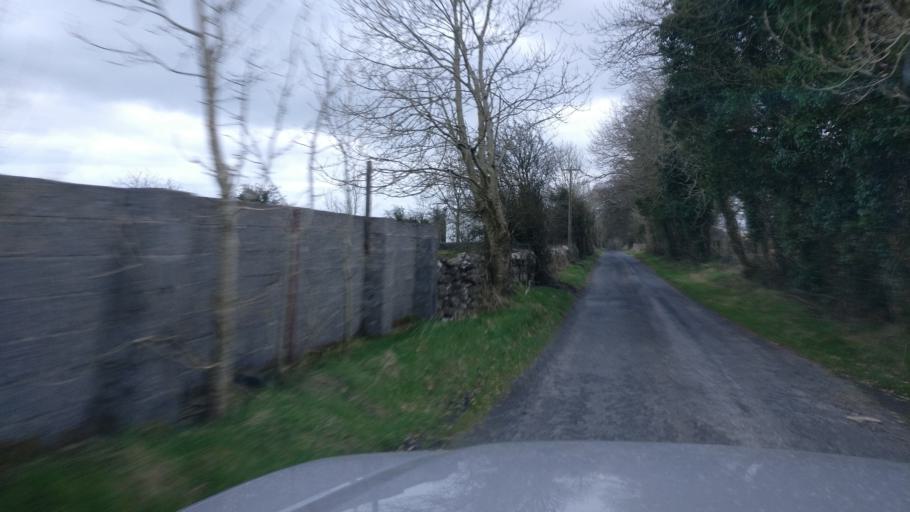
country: IE
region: Connaught
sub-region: County Galway
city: Loughrea
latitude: 53.2645
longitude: -8.4621
